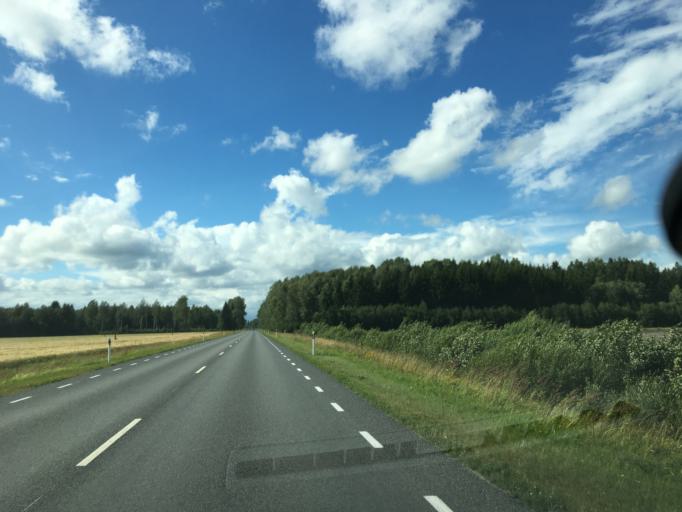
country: EE
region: Paernumaa
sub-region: Vaendra vald (alev)
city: Vandra
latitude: 58.6075
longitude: 25.1220
